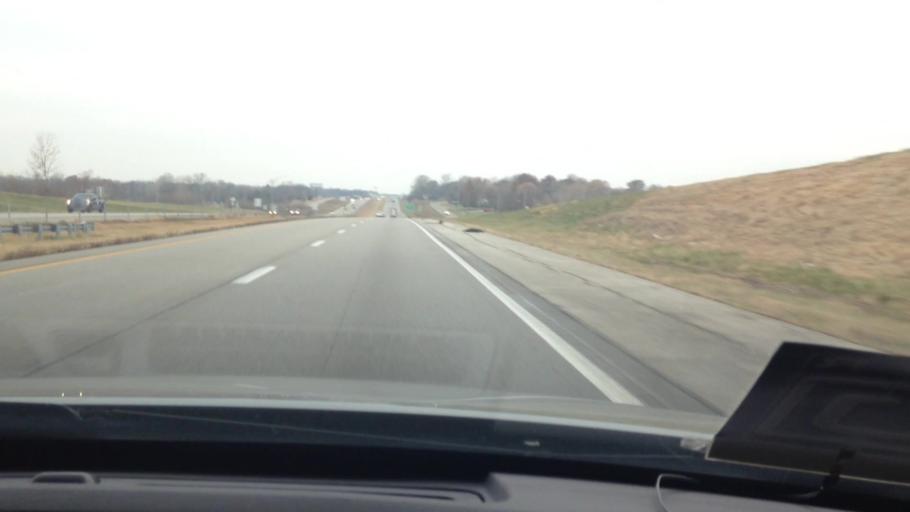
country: US
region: Missouri
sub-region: Cass County
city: Peculiar
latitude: 38.7232
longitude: -94.4549
